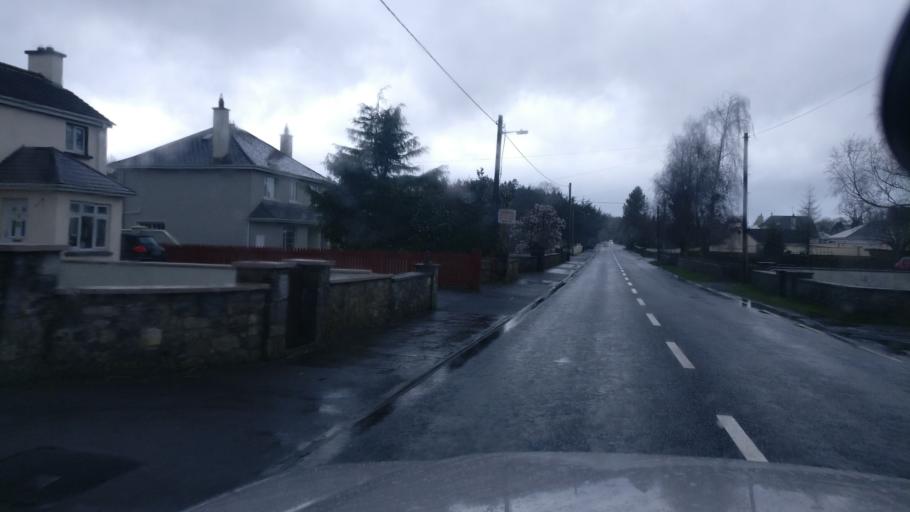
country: IE
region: Connaught
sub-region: County Galway
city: Portumna
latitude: 53.0905
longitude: -8.2364
